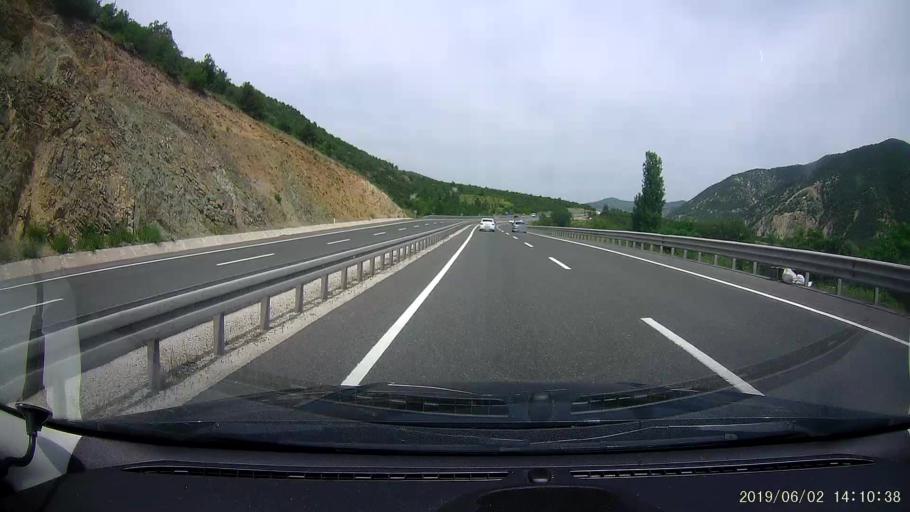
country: TR
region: Cankiri
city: Ilgaz
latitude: 40.9042
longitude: 33.7672
